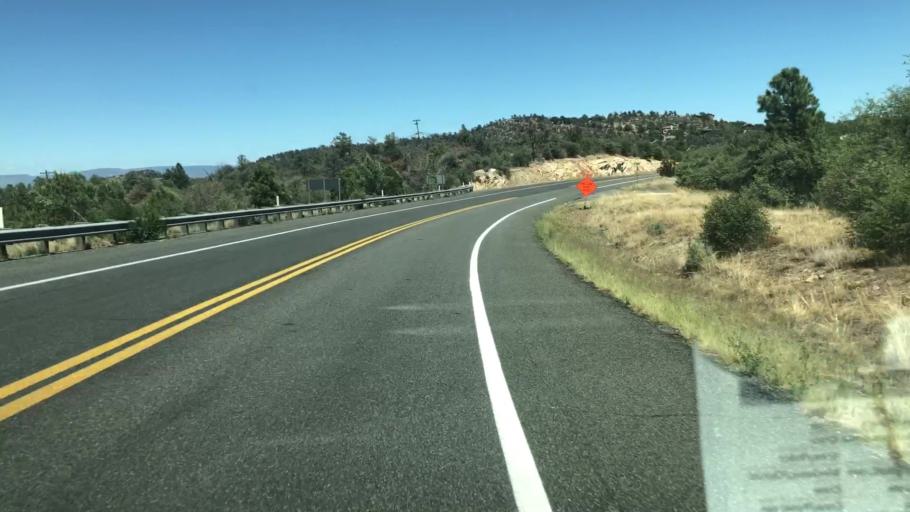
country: US
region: Arizona
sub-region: Yavapai County
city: Prescott
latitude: 34.5784
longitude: -112.5242
